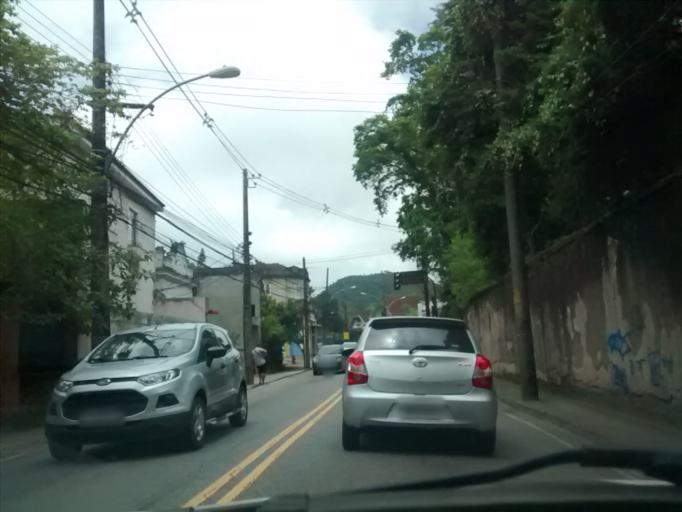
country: BR
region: Rio de Janeiro
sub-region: Rio De Janeiro
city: Rio de Janeiro
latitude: -22.9640
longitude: -43.2761
